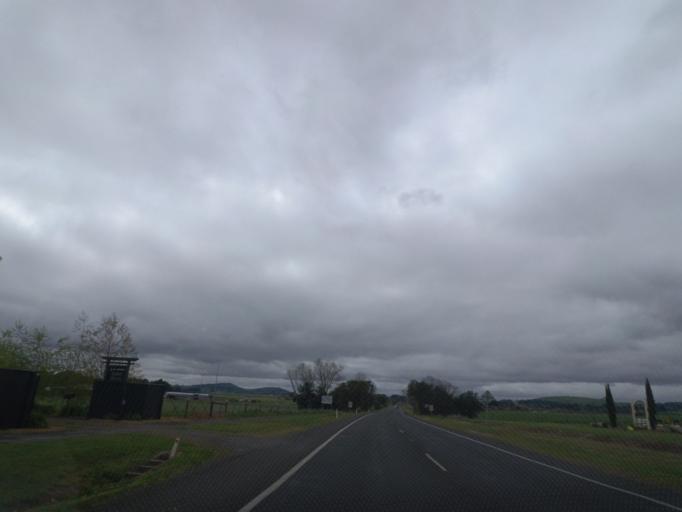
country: AU
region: Victoria
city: Brown Hill
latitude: -37.4098
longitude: 143.9872
